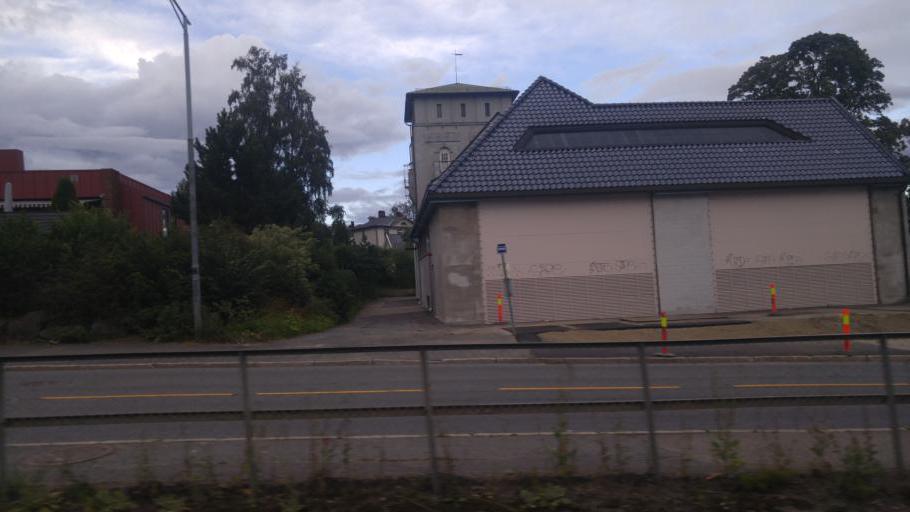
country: NO
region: Oslo
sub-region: Oslo
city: Sjolyststranda
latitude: 59.9483
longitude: 10.7039
